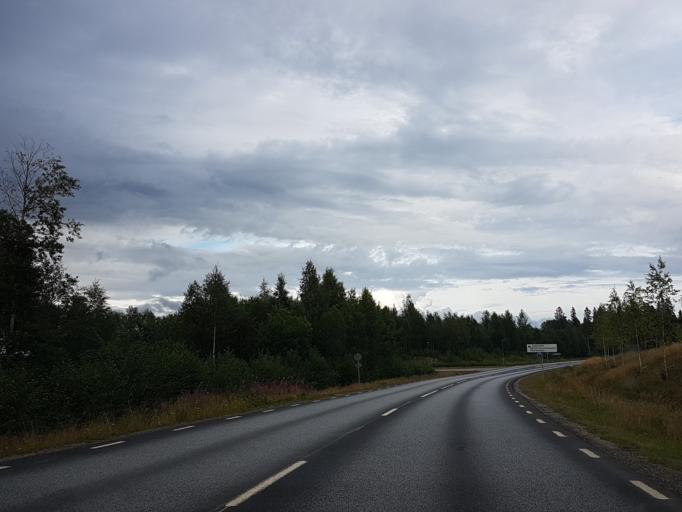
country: SE
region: Vaesterbotten
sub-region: Umea Kommun
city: Ersmark
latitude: 63.8073
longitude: 20.3669
